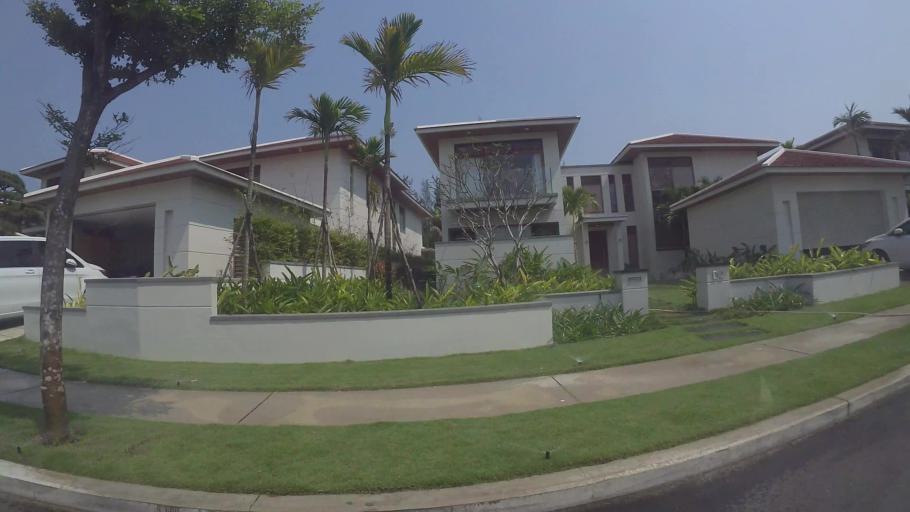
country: VN
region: Da Nang
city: Ngu Hanh Son
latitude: 15.9794
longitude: 108.2795
